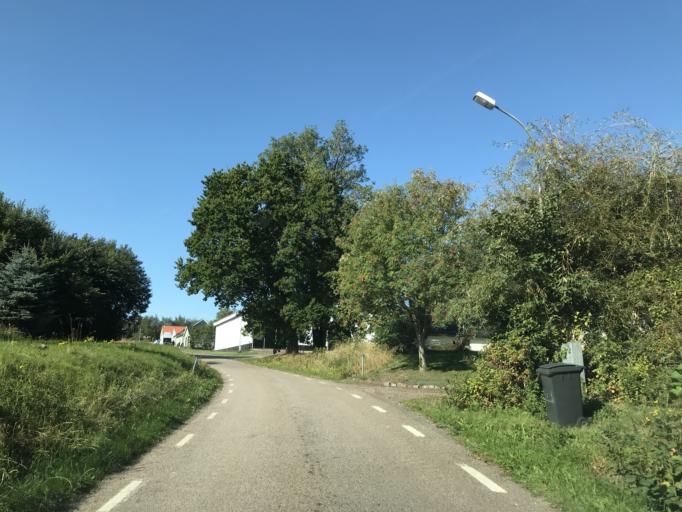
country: SE
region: Skane
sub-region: Landskrona
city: Asmundtorp
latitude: 55.9075
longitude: 12.9437
